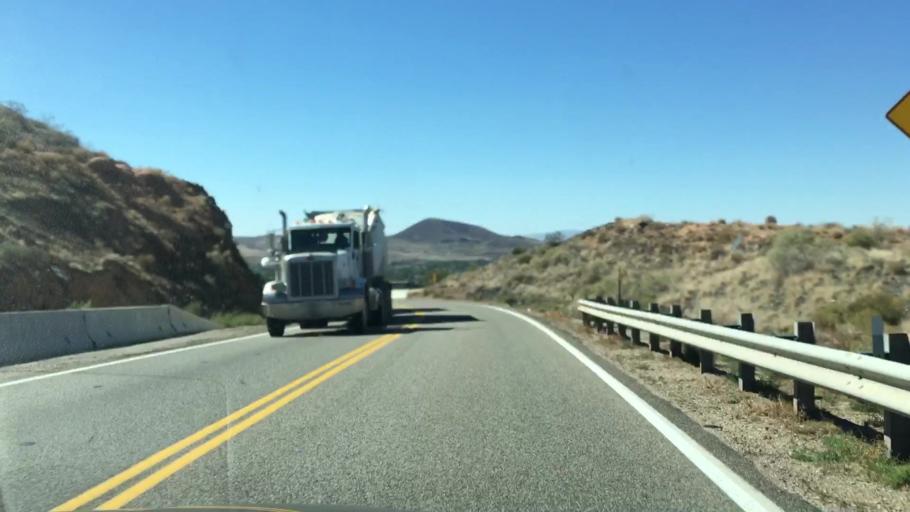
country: US
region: Utah
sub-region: Washington County
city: Hurricane
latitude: 37.1826
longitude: -113.2791
